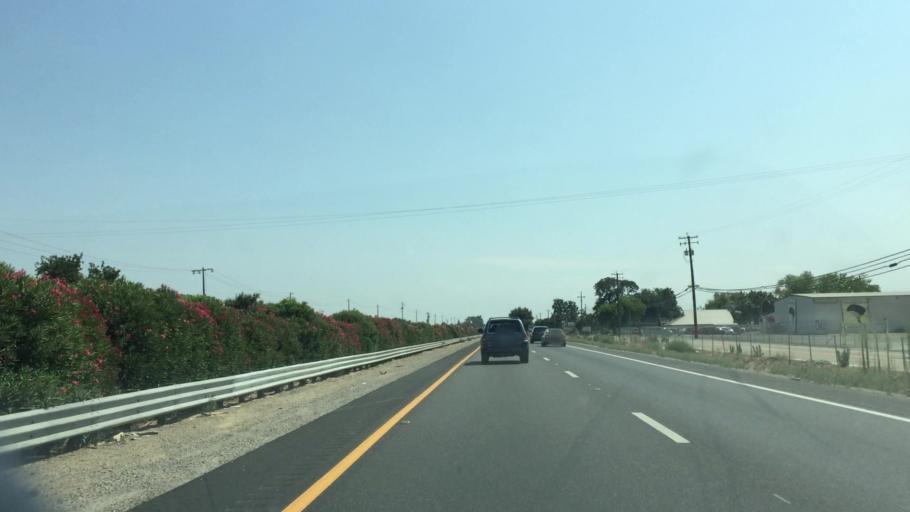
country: US
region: California
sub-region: San Joaquin County
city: Collierville
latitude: 38.2023
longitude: -121.2631
